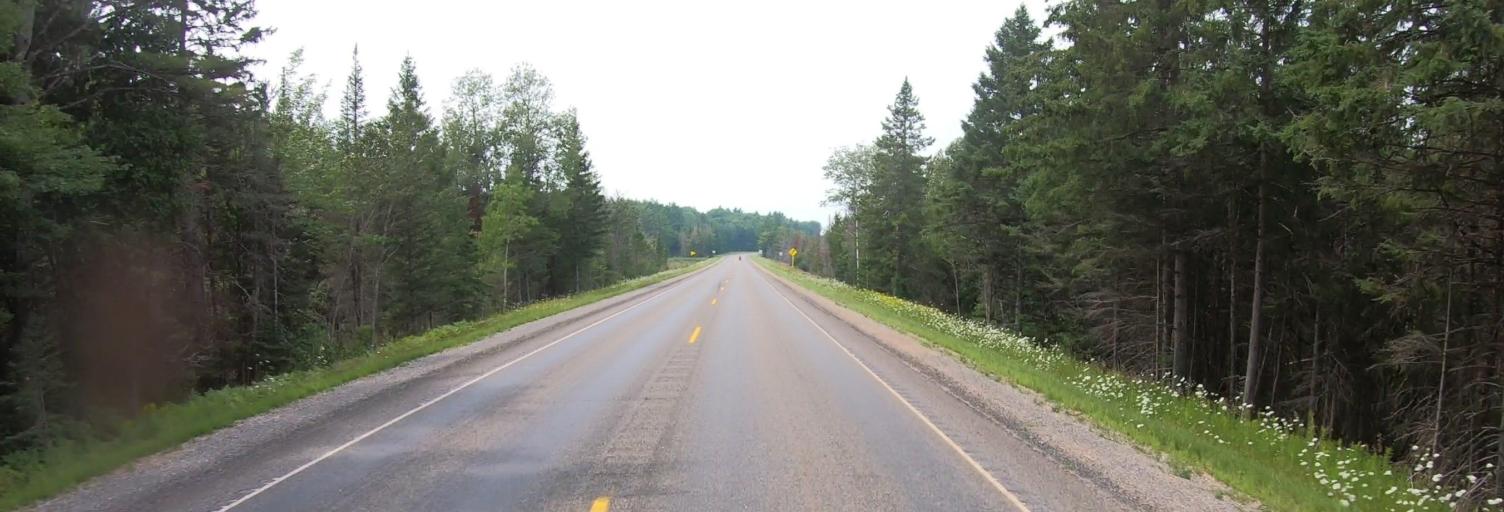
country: US
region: Michigan
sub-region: Alger County
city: Munising
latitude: 46.3329
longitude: -86.8211
